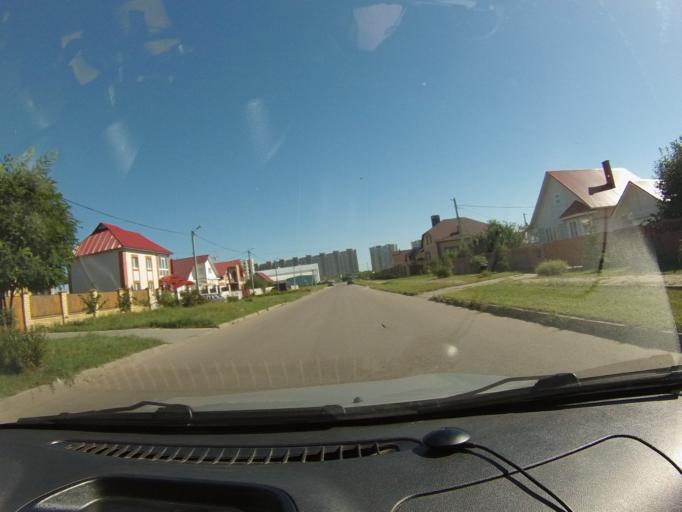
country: RU
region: Tambov
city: Tambov
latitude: 52.7681
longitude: 41.3867
